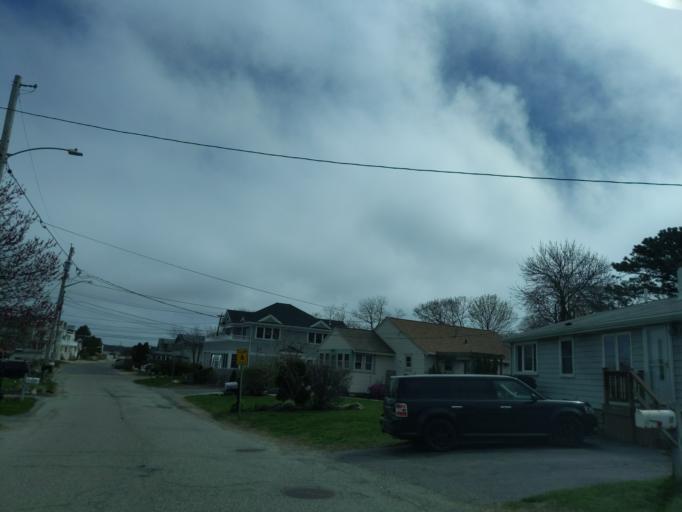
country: US
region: Massachusetts
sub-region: Essex County
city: Rockport
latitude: 42.6251
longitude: -70.6227
